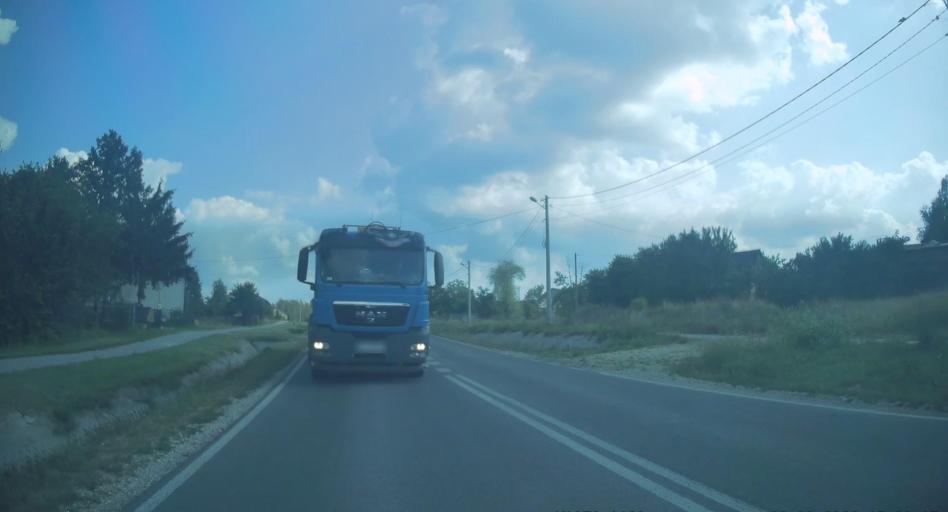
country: PL
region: Swietokrzyskie
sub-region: Powiat konecki
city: Radoszyce
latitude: 51.0392
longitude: 20.2830
